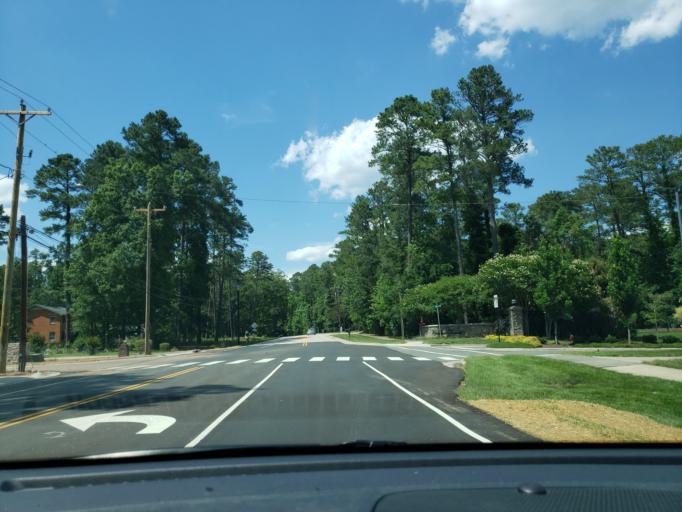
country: US
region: North Carolina
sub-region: Durham County
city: Durham
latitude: 35.9820
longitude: -78.9899
